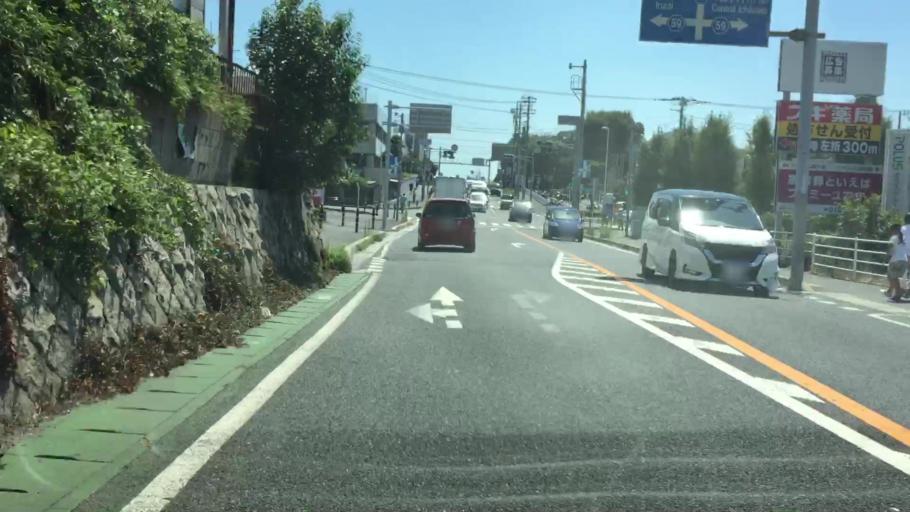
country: JP
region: Chiba
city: Funabashi
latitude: 35.7283
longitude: 139.9594
